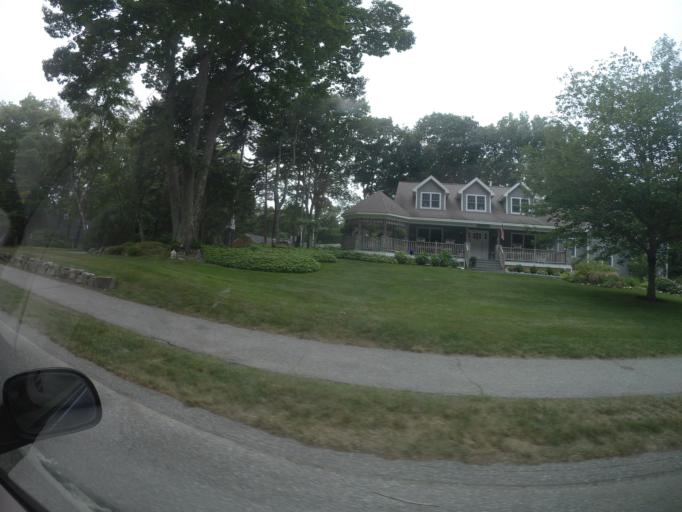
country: US
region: Maine
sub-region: York County
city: Kennebunkport
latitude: 43.3519
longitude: -70.4793
